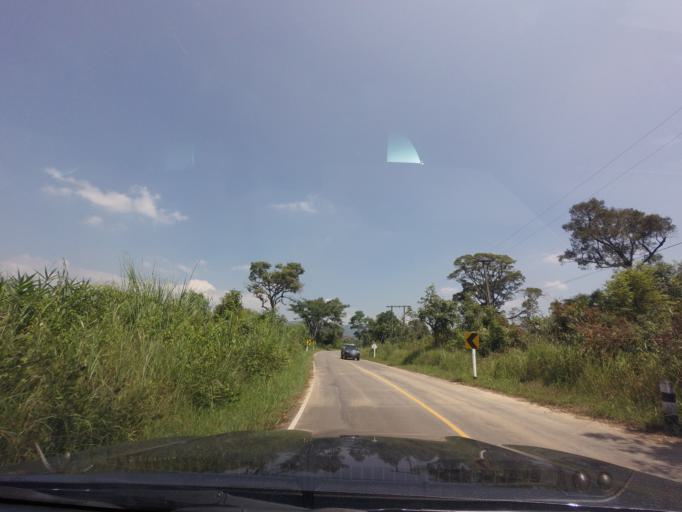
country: TH
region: Loei
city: Na Haeo
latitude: 17.5737
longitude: 100.8975
